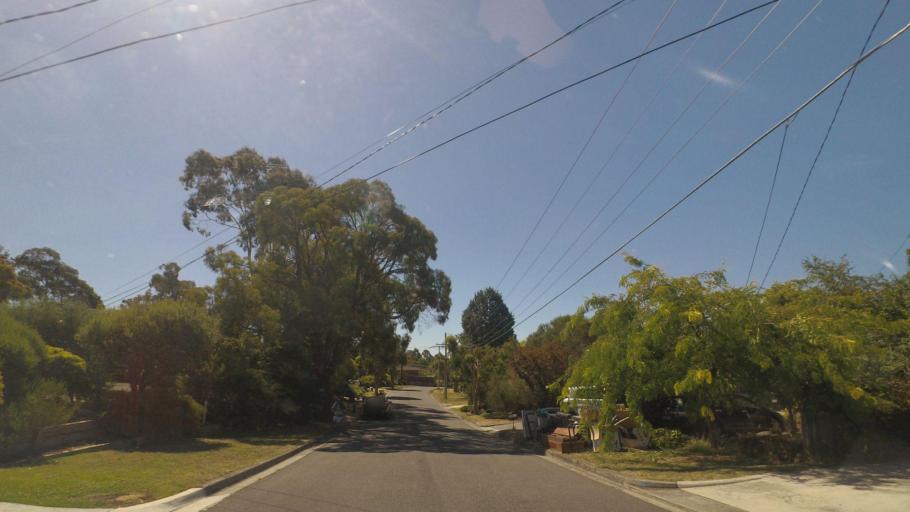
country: AU
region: Victoria
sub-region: Yarra Ranges
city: Chirnside Park
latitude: -37.7468
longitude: 145.3291
